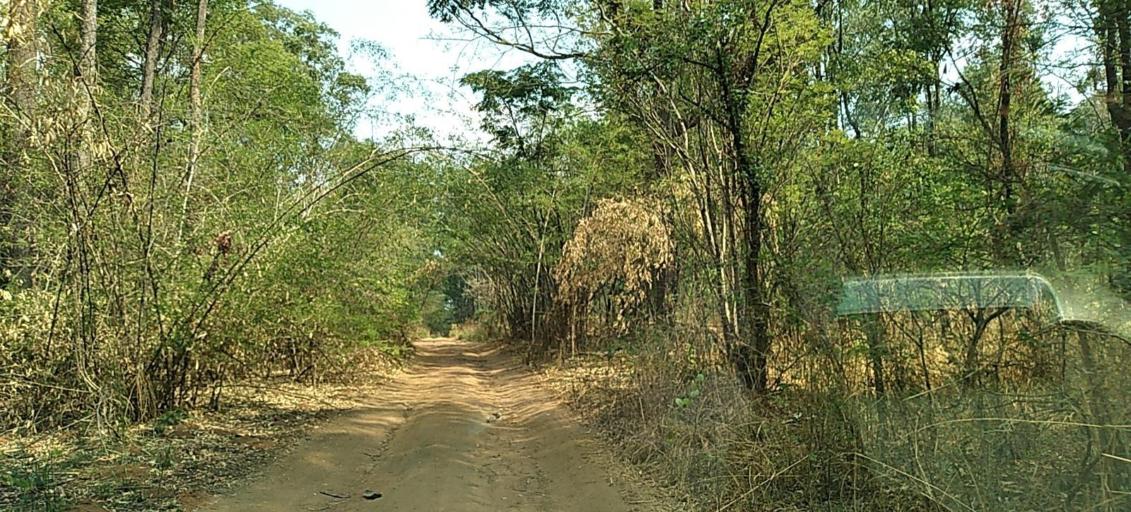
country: ZM
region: Copperbelt
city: Chingola
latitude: -12.7373
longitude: 27.7583
